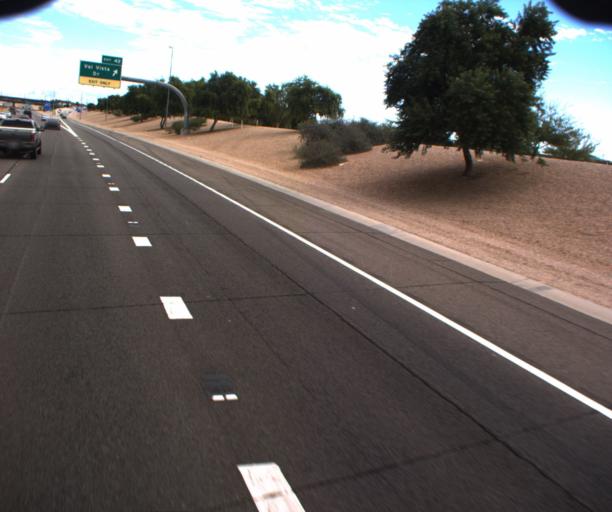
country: US
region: Arizona
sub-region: Maricopa County
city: Gilbert
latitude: 33.2847
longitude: -111.7618
